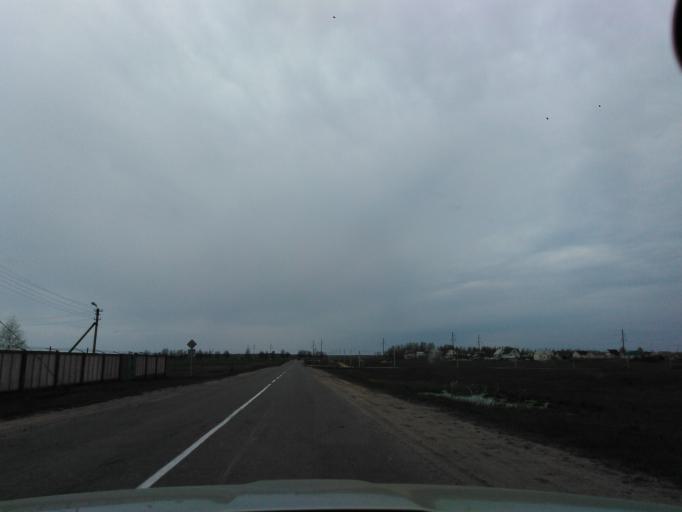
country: BY
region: Vitebsk
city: Chashniki
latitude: 54.8397
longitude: 29.1607
